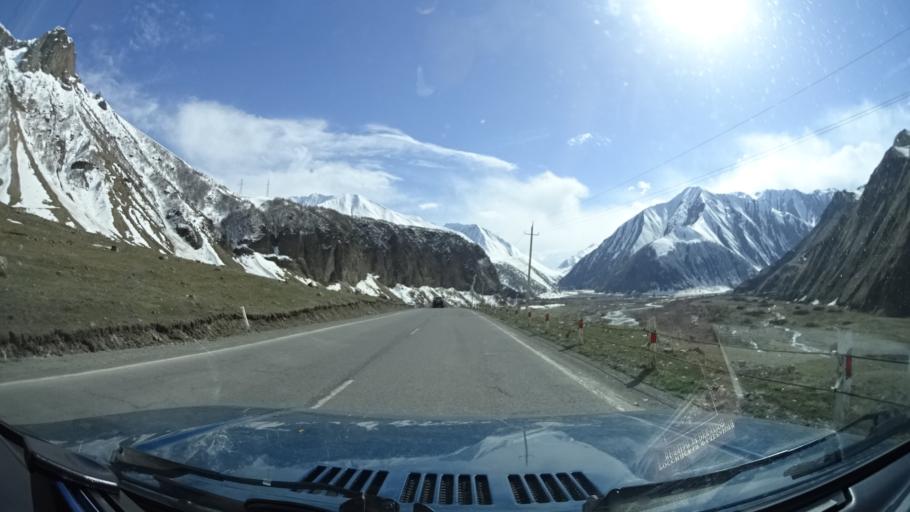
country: GE
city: Gudauri
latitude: 42.5701
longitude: 44.5214
